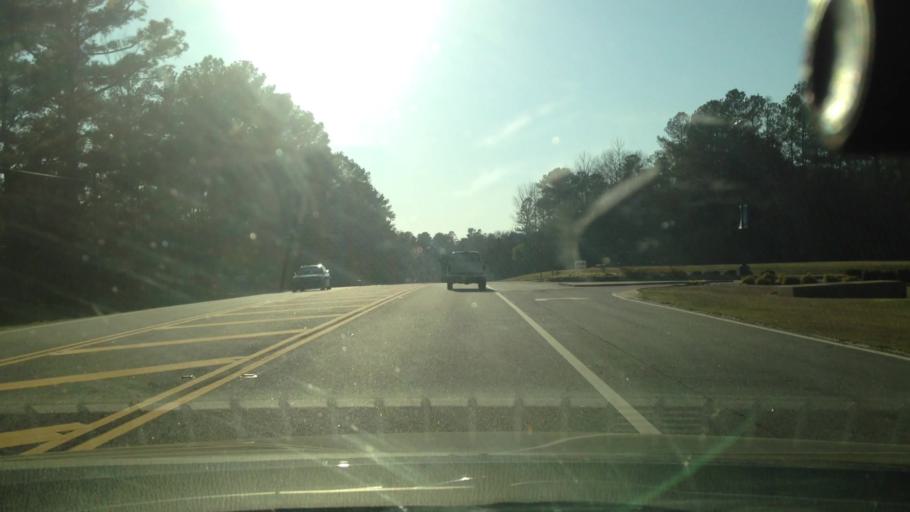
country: US
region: Georgia
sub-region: Coweta County
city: East Newnan
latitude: 33.3398
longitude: -84.6803
